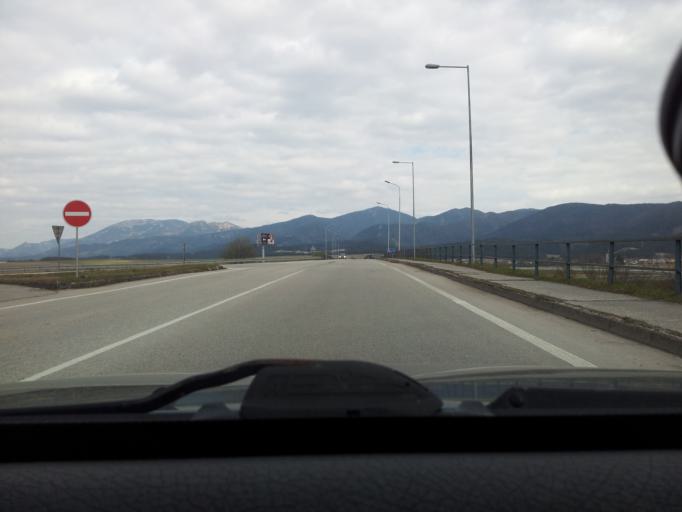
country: SK
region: Banskobystricky
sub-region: Okres Ziar nad Hronom
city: Kremnica
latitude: 48.8640
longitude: 18.8647
